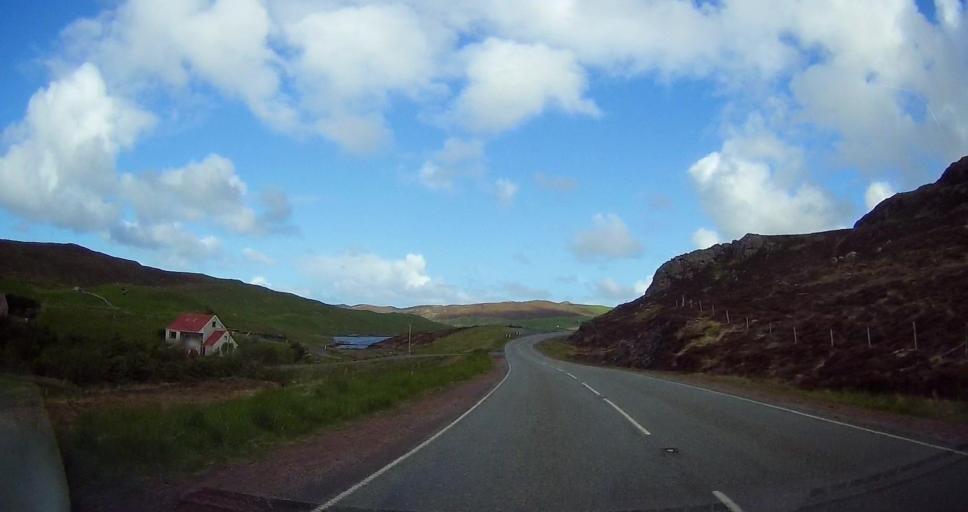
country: GB
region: Scotland
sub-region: Shetland Islands
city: Lerwick
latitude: 60.4057
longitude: -1.3866
